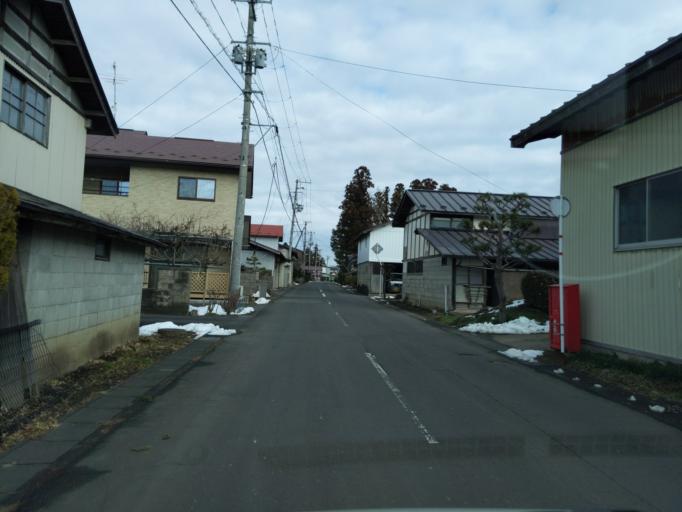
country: JP
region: Iwate
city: Mizusawa
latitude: 39.0851
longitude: 141.1709
